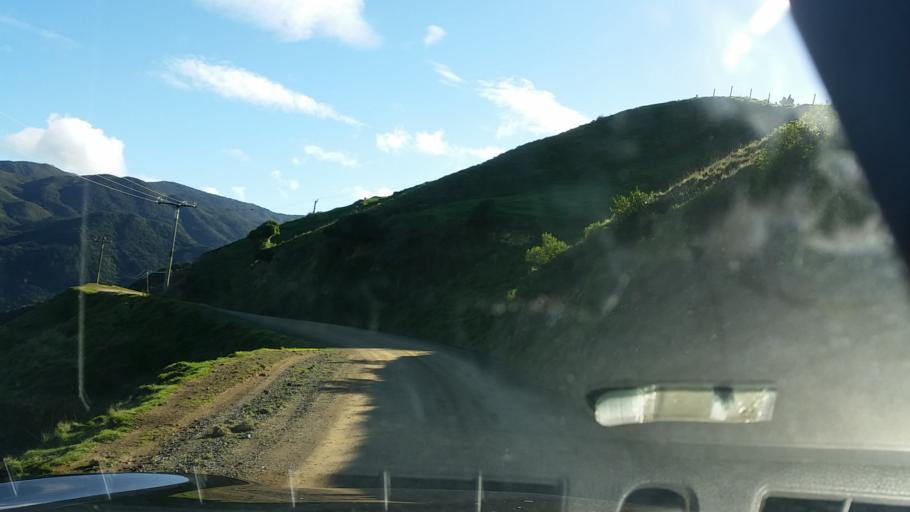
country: NZ
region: Marlborough
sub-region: Marlborough District
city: Picton
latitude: -40.9302
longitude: 173.8402
